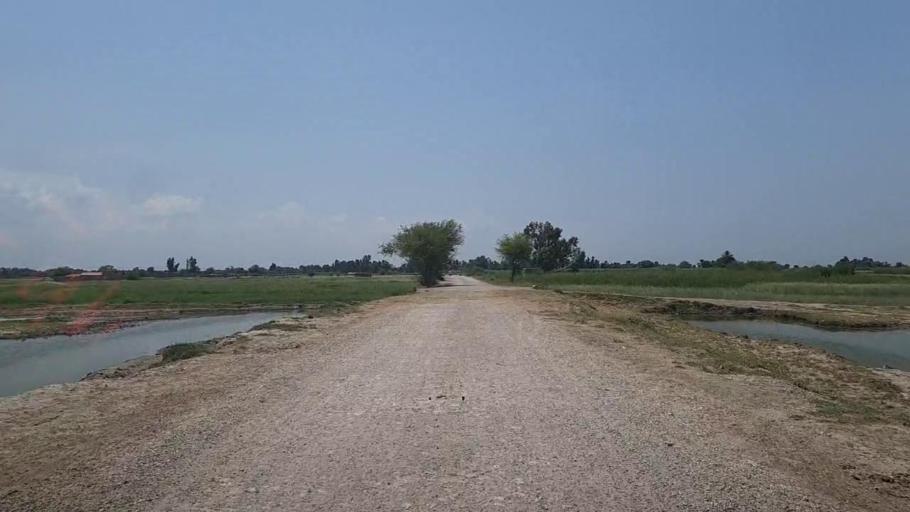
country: PK
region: Sindh
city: Ubauro
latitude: 28.1572
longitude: 69.7643
